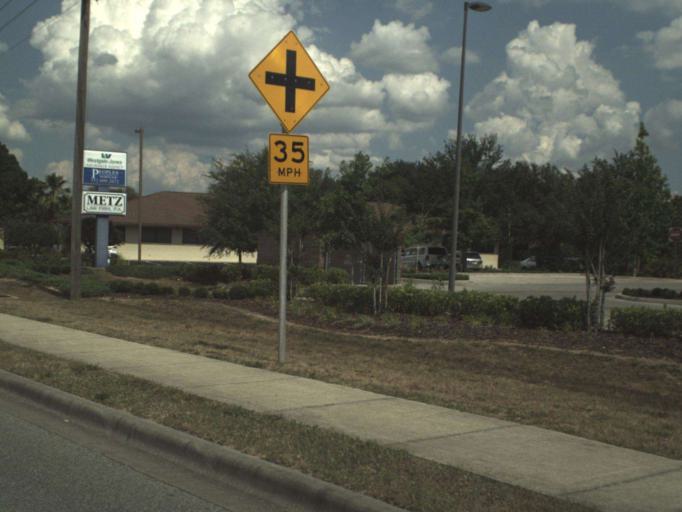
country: US
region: Florida
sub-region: Lake County
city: Eustis
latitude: 28.8228
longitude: -81.6932
